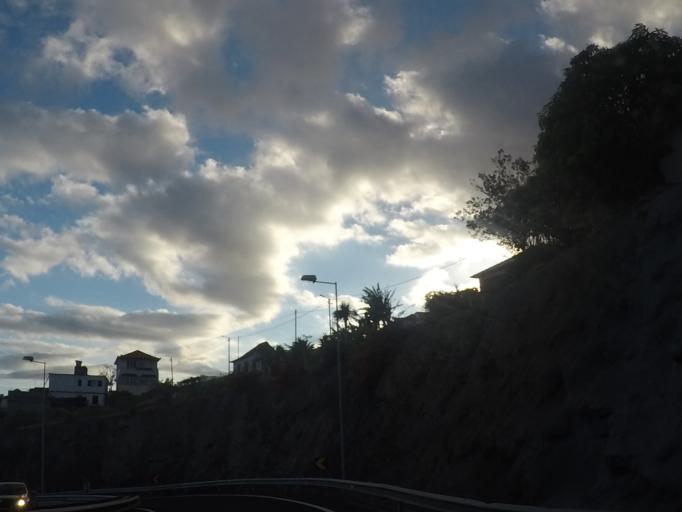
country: PT
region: Madeira
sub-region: Santa Cruz
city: Santa Cruz
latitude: 32.6570
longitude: -16.8144
